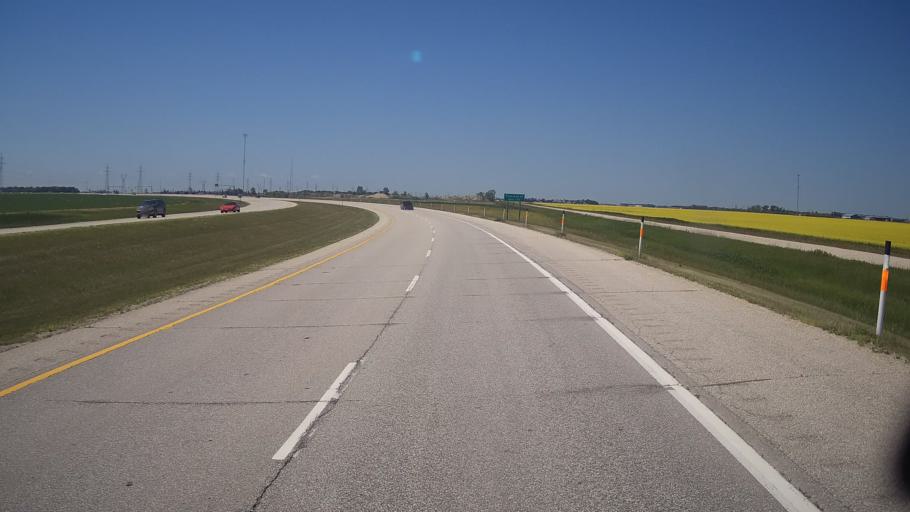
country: CA
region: Manitoba
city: Stonewall
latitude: 49.9900
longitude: -97.3003
